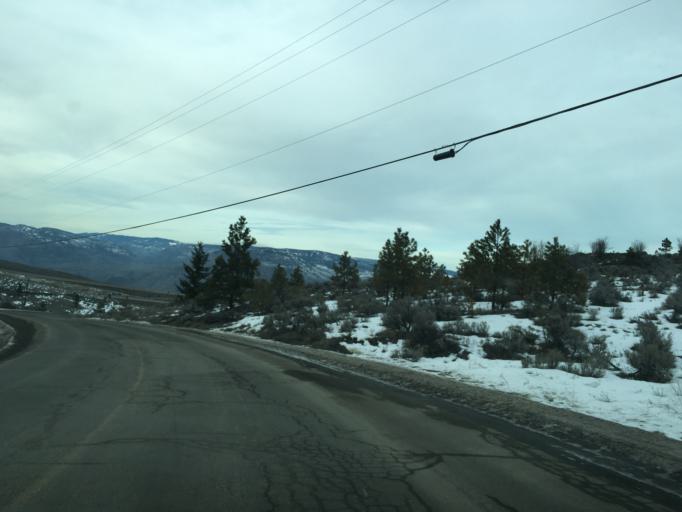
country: CA
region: British Columbia
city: Kamloops
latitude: 50.6597
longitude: -120.4350
